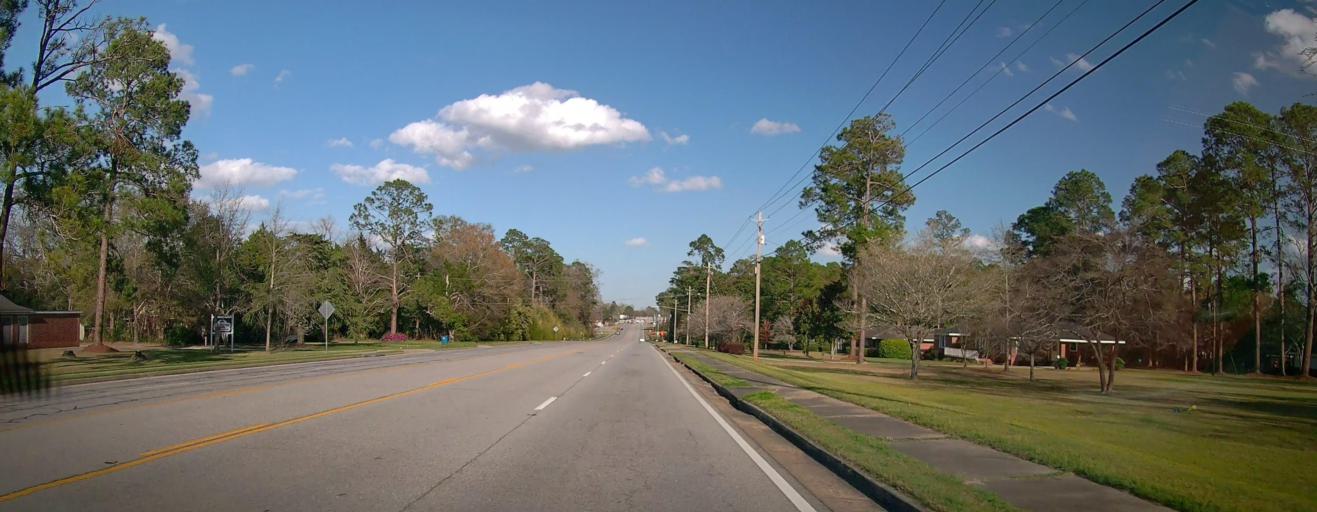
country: US
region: Georgia
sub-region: Toombs County
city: Vidalia
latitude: 32.2200
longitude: -82.4311
